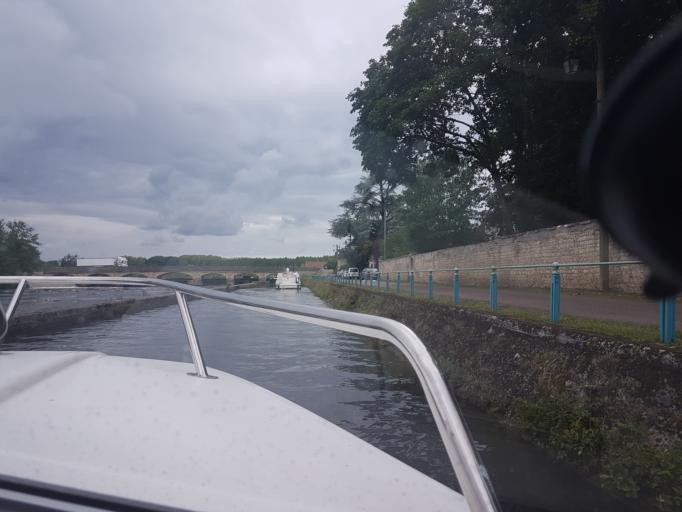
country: FR
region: Bourgogne
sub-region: Departement de l'Yonne
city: Champs-sur-Yonne
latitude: 47.7338
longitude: 3.5995
